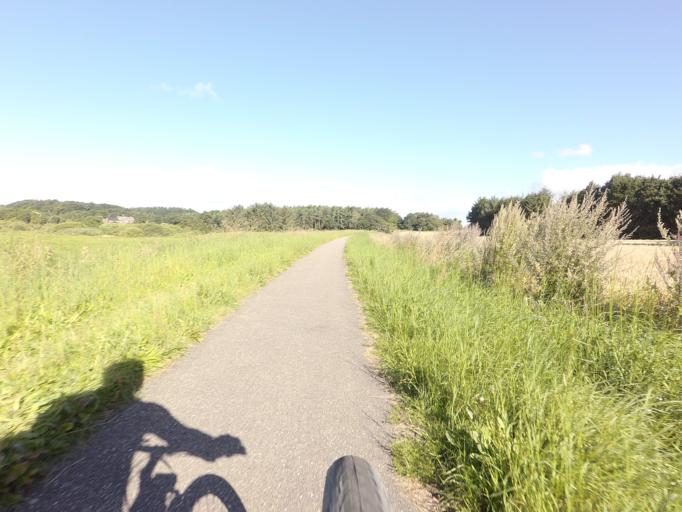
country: DK
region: Central Jutland
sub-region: Horsens Kommune
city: Horsens
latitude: 55.9532
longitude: 9.7750
